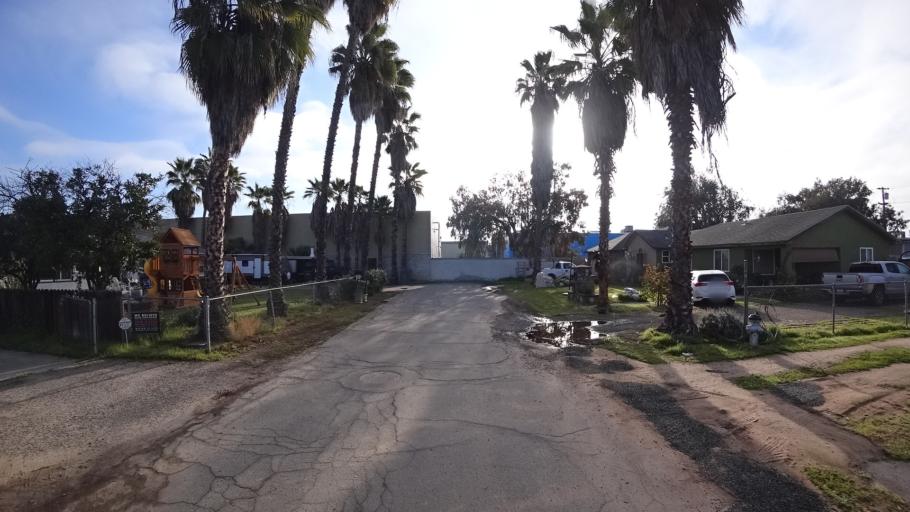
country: US
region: California
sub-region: Fresno County
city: Fresno
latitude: 36.8194
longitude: -119.7926
